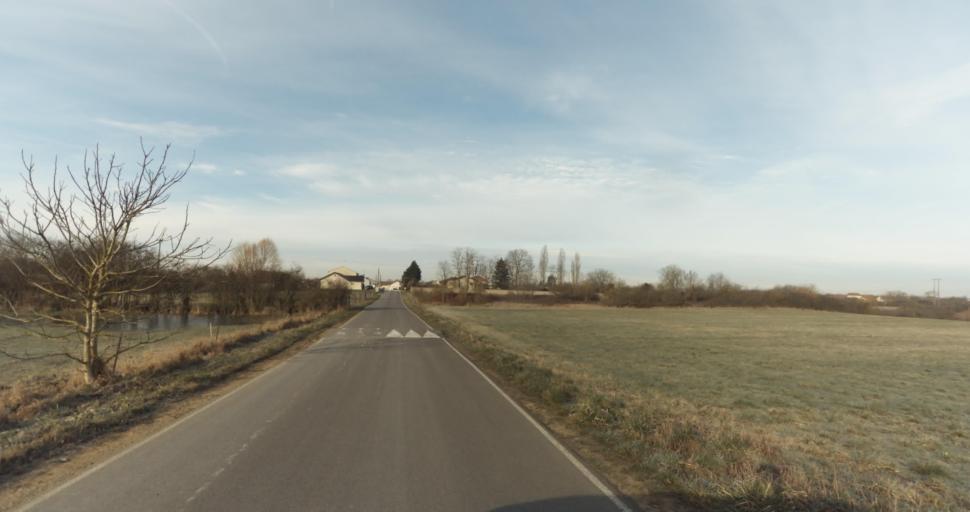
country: FR
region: Lorraine
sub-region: Departement de Meurthe-et-Moselle
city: Jarny
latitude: 49.1598
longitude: 5.8963
